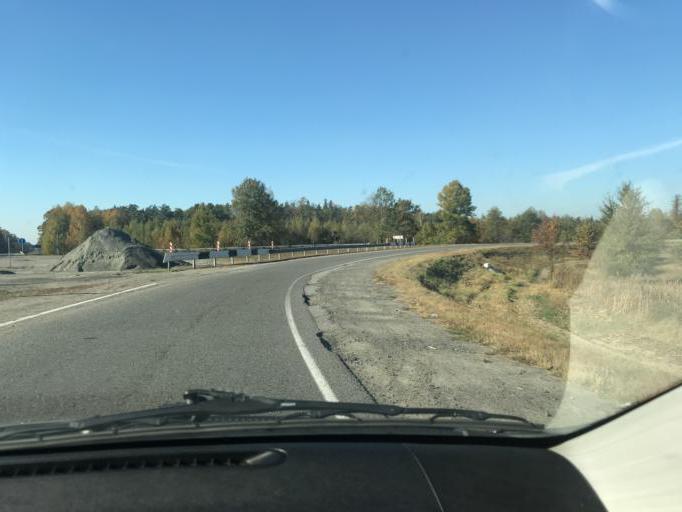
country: BY
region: Brest
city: Mikashevichy
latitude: 52.2439
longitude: 27.4432
